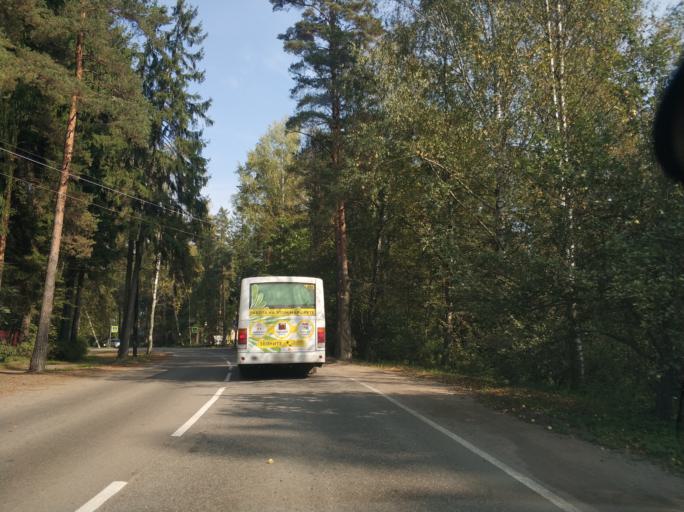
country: RU
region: Leningrad
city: Vsevolozhsk
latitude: 60.0105
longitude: 30.6189
